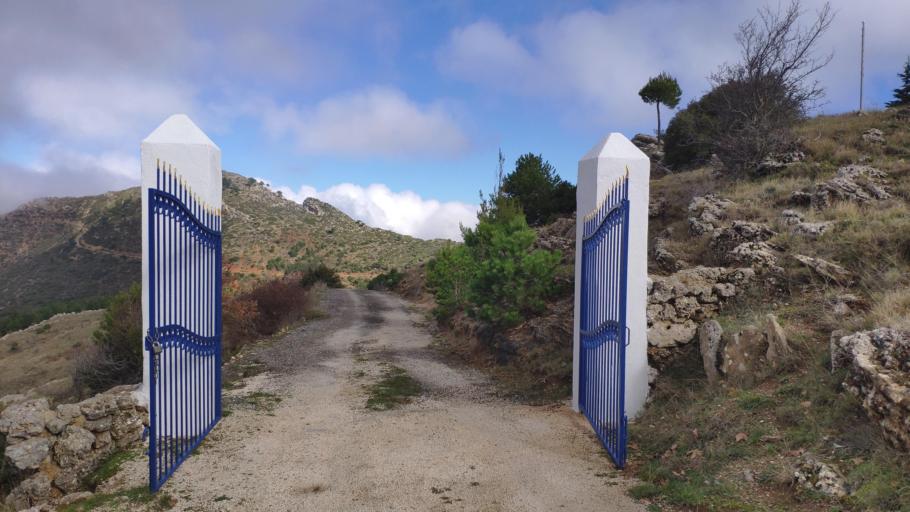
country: GR
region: West Greece
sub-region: Nomos Achaias
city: Aiyira
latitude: 38.0576
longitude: 22.4400
